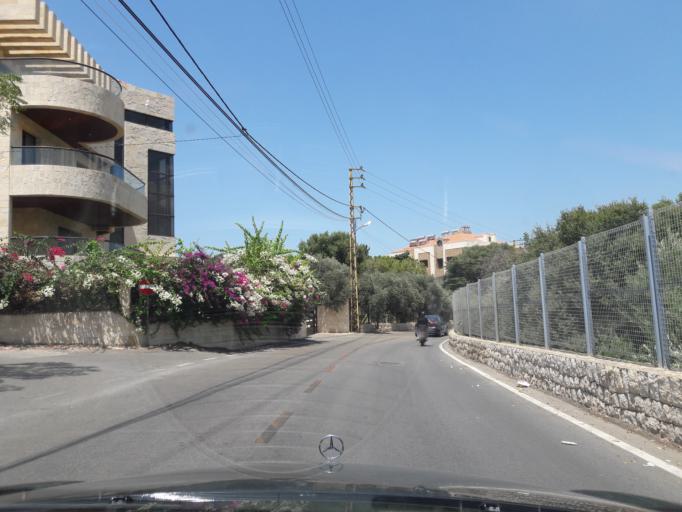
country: LB
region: Mont-Liban
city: Djounie
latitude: 33.9310
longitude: 35.6249
